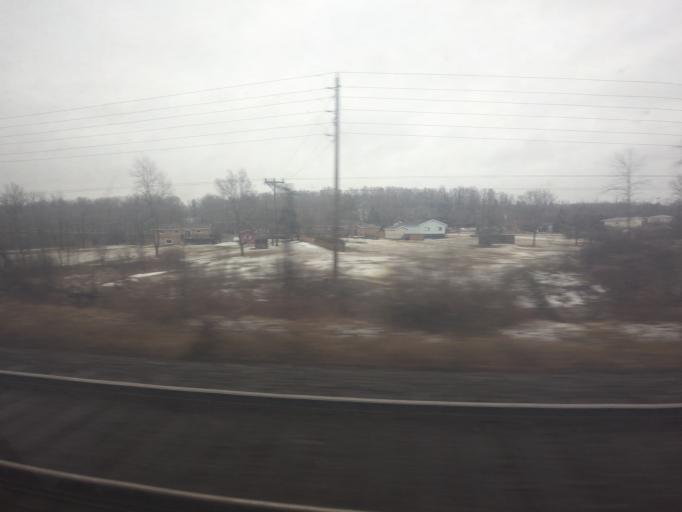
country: CA
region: Ontario
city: Kingston
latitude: 44.2952
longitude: -76.4275
